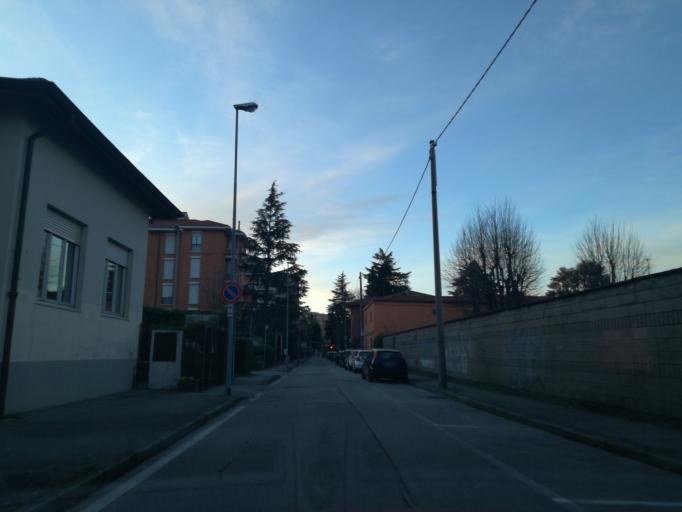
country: IT
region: Lombardy
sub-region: Provincia di Monza e Brianza
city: Vimercate
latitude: 45.6176
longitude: 9.3684
